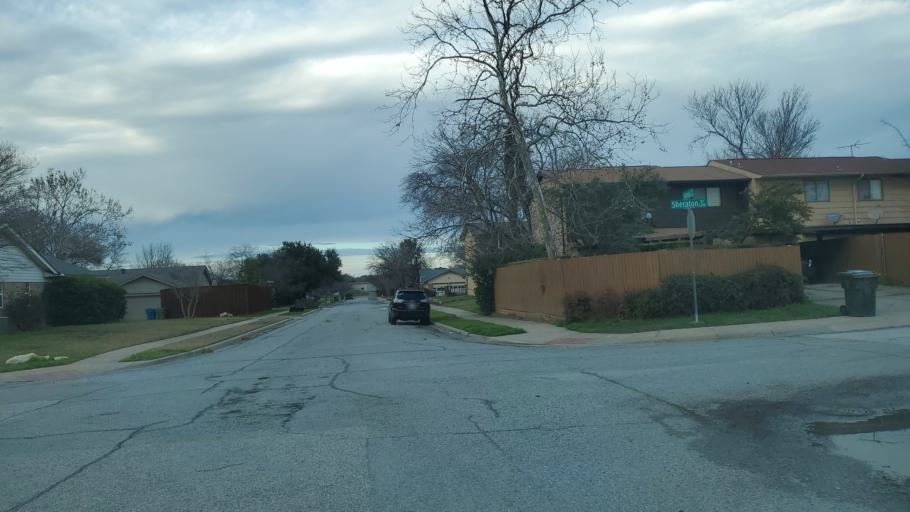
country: US
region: Texas
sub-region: Dallas County
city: Carrollton
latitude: 32.9910
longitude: -96.8795
